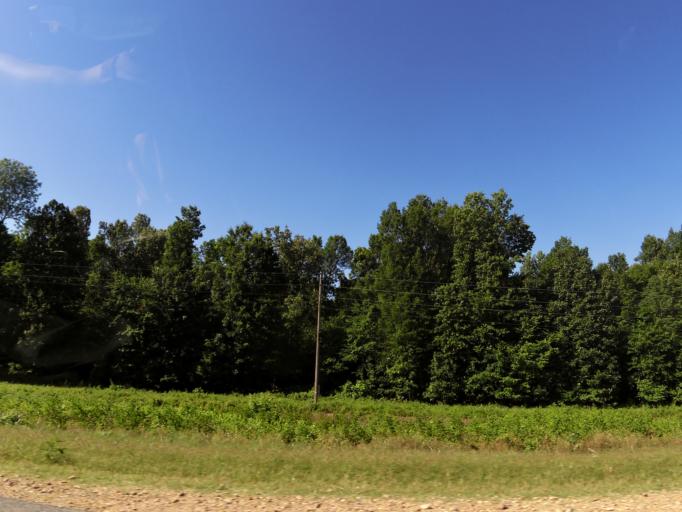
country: US
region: Arkansas
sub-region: Clay County
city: Corning
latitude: 36.4009
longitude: -90.5386
